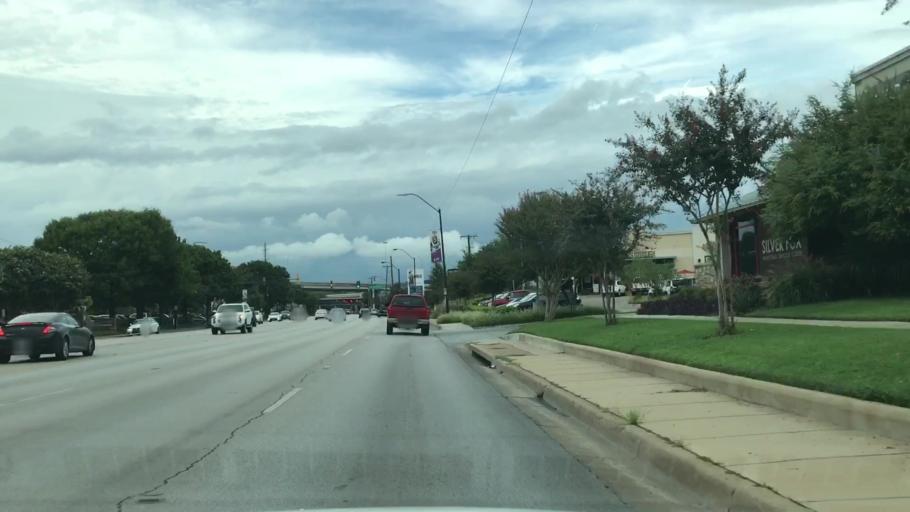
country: US
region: Texas
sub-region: Tarrant County
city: Fort Worth
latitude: 32.7270
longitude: -97.3611
